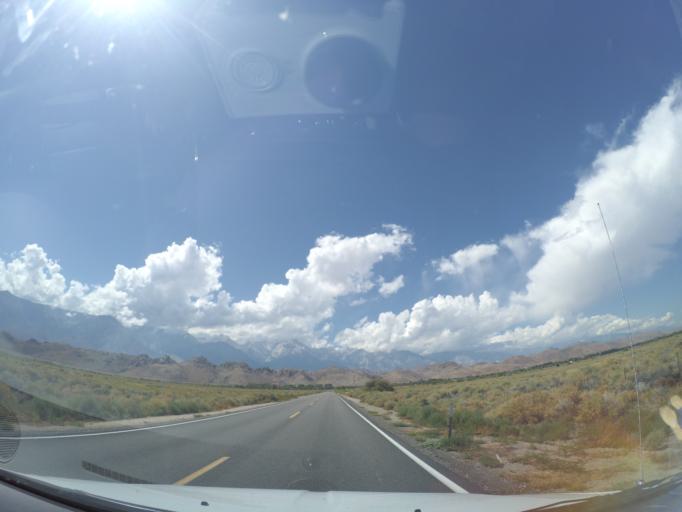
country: US
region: California
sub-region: Inyo County
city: Lone Pine
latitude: 36.5793
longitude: -118.0439
